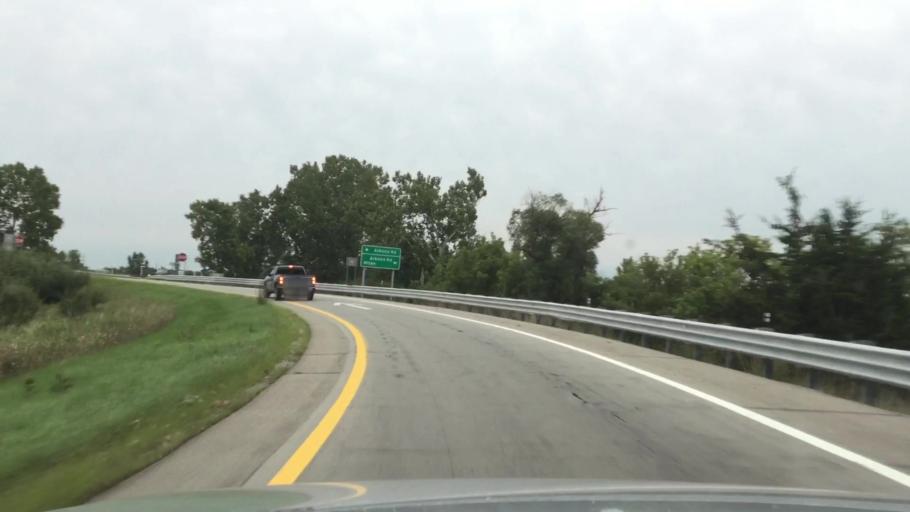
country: US
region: Michigan
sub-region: Washtenaw County
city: Milan
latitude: 42.1001
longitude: -83.6777
